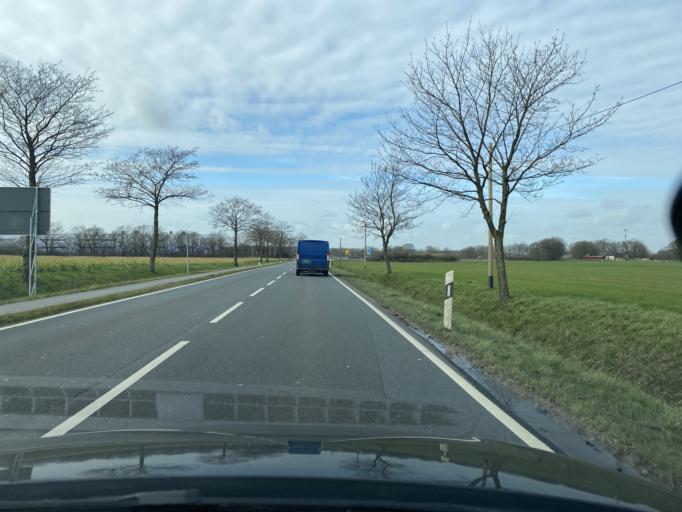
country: DE
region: North Rhine-Westphalia
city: Oelde
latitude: 51.8348
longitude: 8.2109
